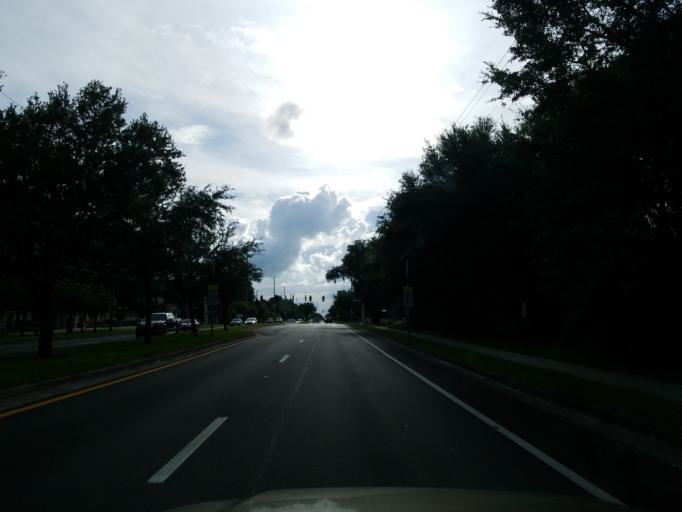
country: US
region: Florida
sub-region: Hillsborough County
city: Bloomingdale
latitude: 27.8938
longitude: -82.2529
